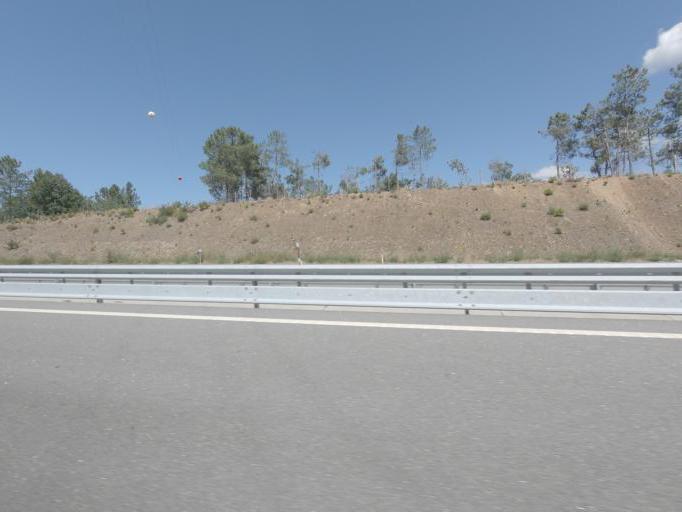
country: PT
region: Vila Real
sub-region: Santa Marta de Penaguiao
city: Santa Marta de Penaguiao
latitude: 41.2733
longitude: -7.8180
